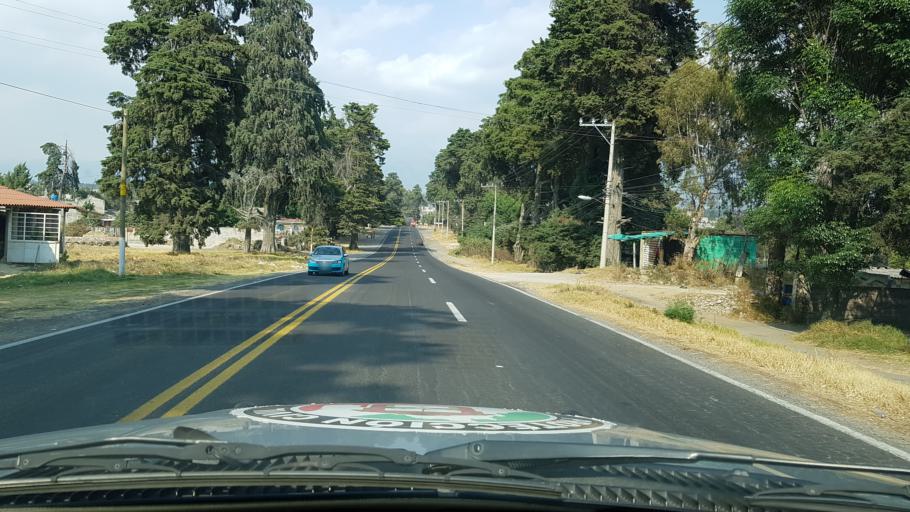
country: MX
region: Mexico
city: Ozumba de Alzate
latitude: 19.0415
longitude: -98.8022
